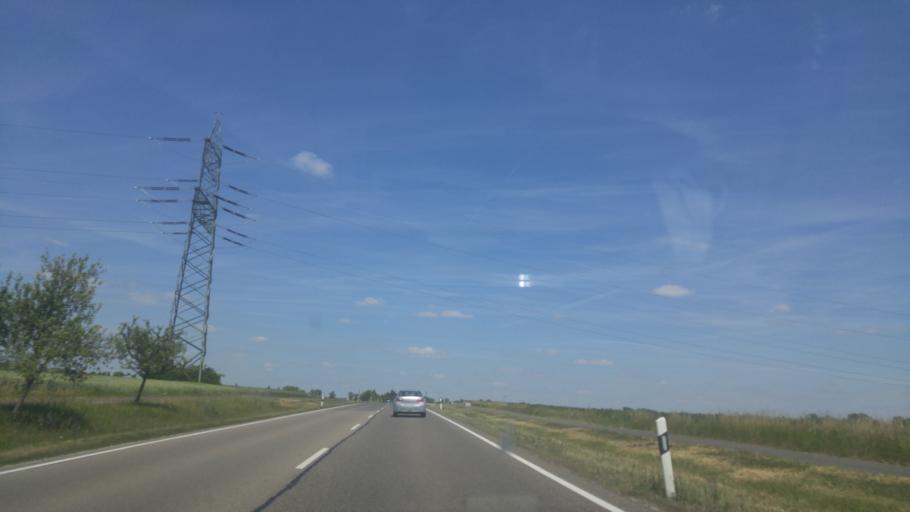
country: DE
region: Bavaria
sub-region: Regierungsbezirk Mittelfranken
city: Illesheim
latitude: 49.4861
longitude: 10.3877
